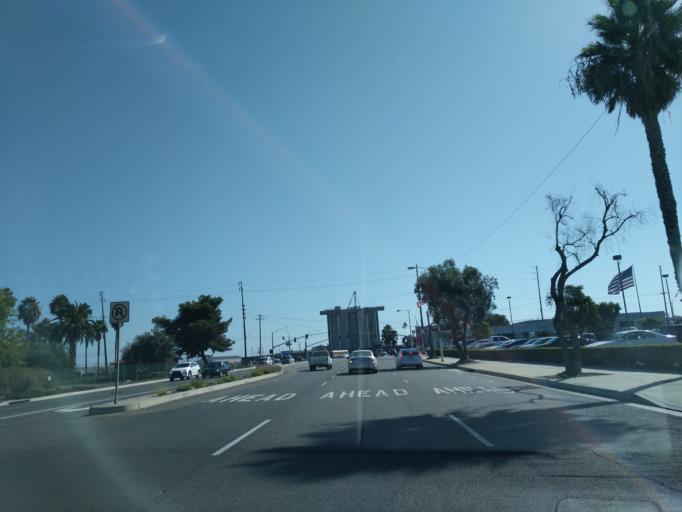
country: US
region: California
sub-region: Orange County
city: Rossmoor
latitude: 33.7611
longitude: -118.0778
